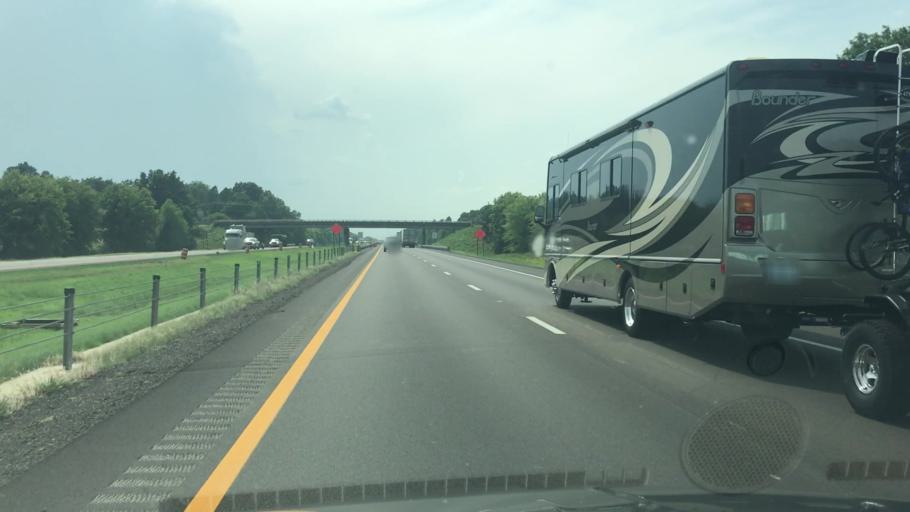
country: US
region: Arkansas
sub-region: Crittenden County
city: Earle
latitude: 35.1342
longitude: -90.4420
